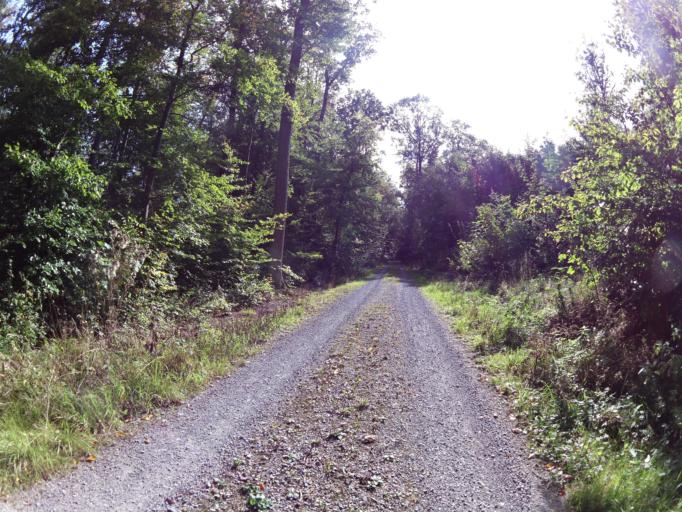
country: DE
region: Bavaria
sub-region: Regierungsbezirk Unterfranken
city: Waldbrunn
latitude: 49.7251
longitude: 9.8032
